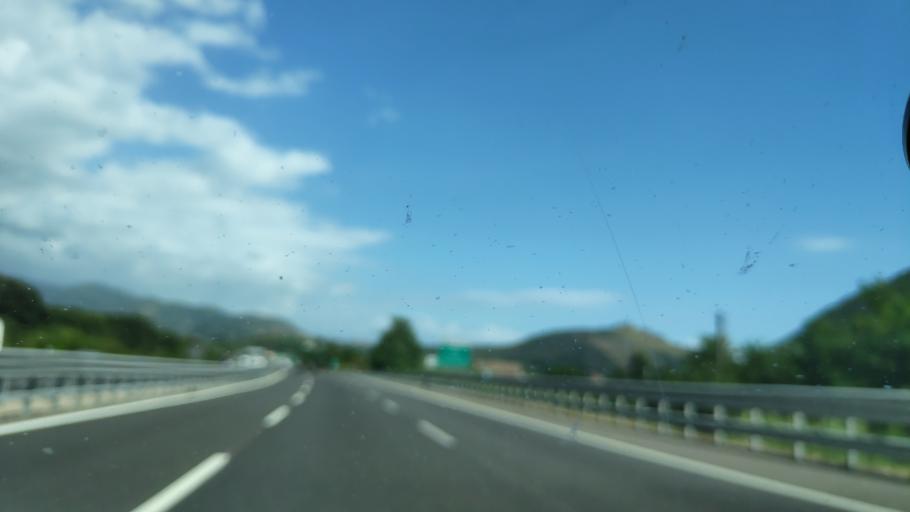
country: IT
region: Campania
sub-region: Provincia di Salerno
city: San Mango Piemonte
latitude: 40.6882
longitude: 14.8423
